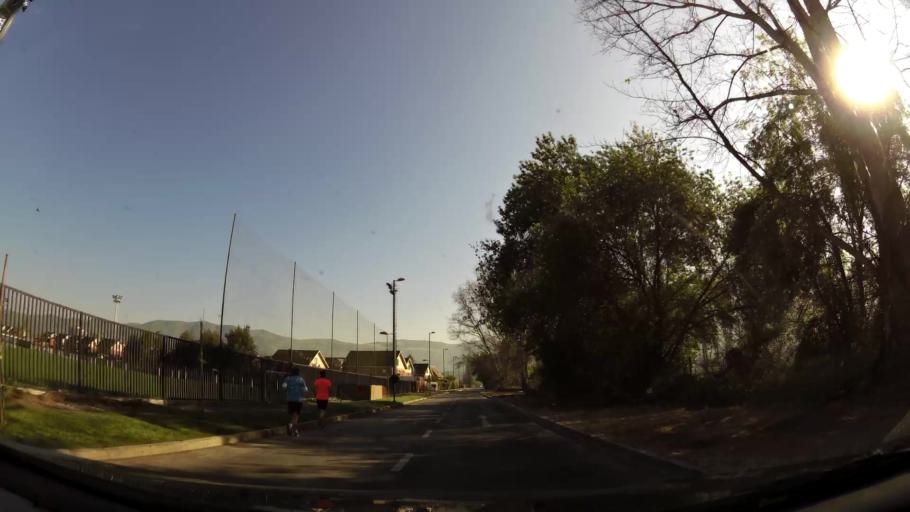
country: CL
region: Santiago Metropolitan
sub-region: Provincia de Chacabuco
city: Chicureo Abajo
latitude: -33.3618
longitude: -70.6644
